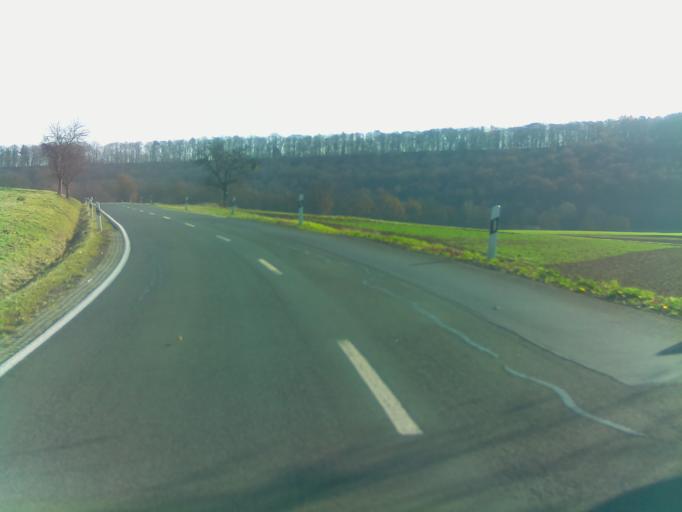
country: DE
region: Bavaria
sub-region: Regierungsbezirk Unterfranken
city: Niederlauer
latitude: 50.2917
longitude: 10.1539
